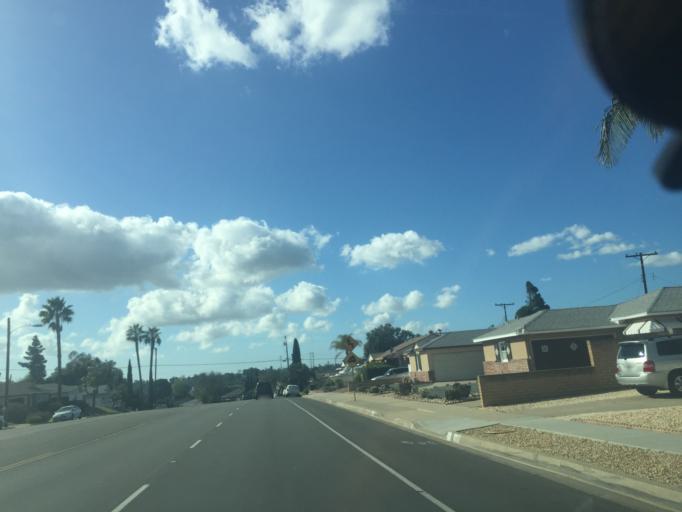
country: US
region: California
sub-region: San Diego County
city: La Mesa
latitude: 32.7902
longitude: -117.0834
